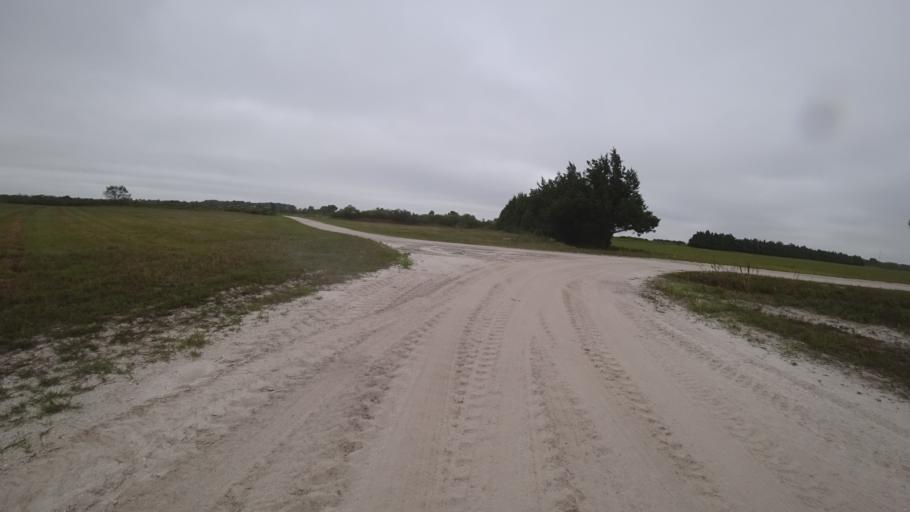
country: US
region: Florida
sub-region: Sarasota County
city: Warm Mineral Springs
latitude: 27.2996
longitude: -82.1346
